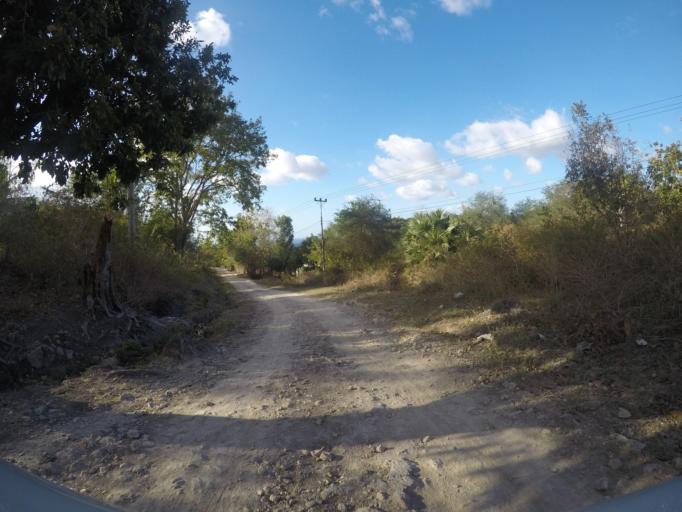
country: TL
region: Lautem
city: Lospalos
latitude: -8.4337
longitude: 126.8487
